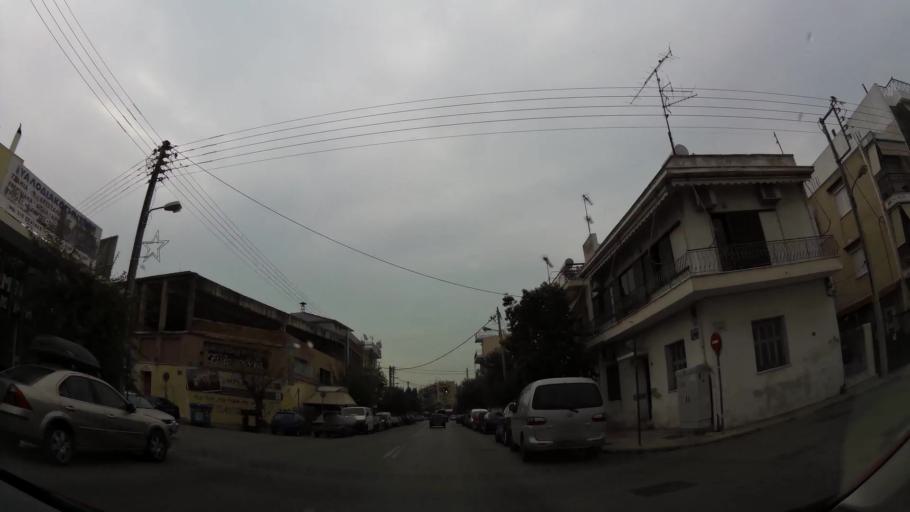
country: GR
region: Attica
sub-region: Nomarchia Athinas
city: Peristeri
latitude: 38.0112
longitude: 23.7018
